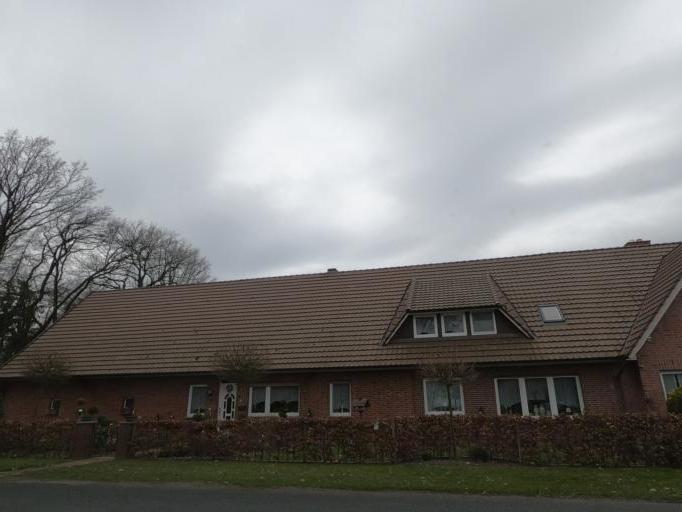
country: DE
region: Lower Saxony
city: Molbergen
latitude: 52.8701
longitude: 7.9249
